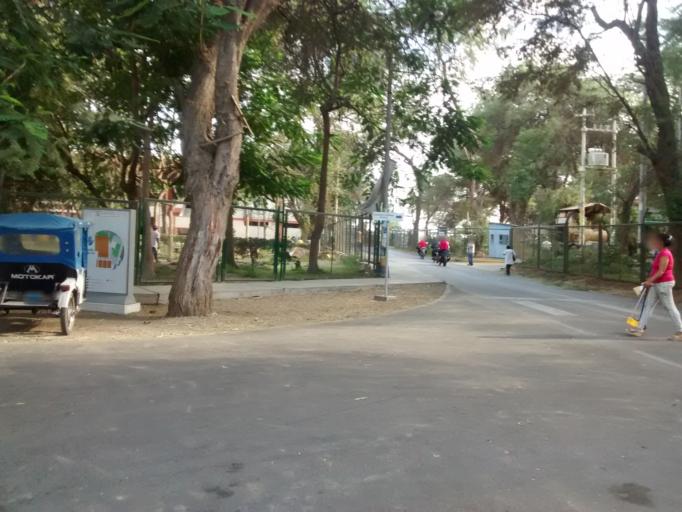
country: PE
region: Piura
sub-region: Provincia de Piura
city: Piura
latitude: -5.1783
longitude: -80.6198
